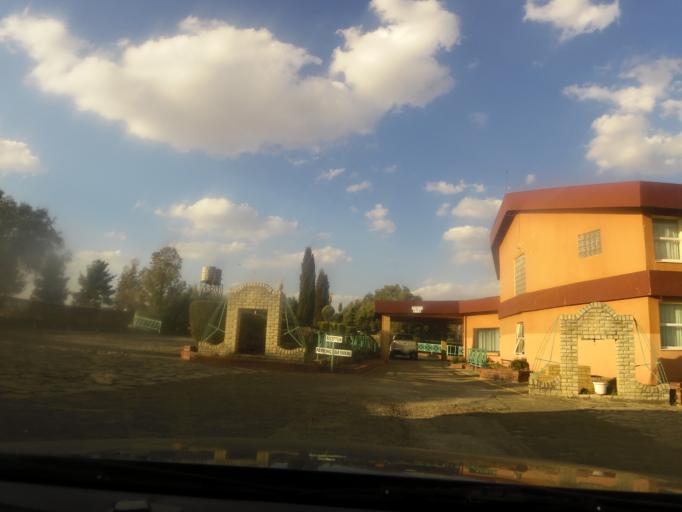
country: LS
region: Berea
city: Teyateyaneng
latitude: -29.1681
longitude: 27.6390
